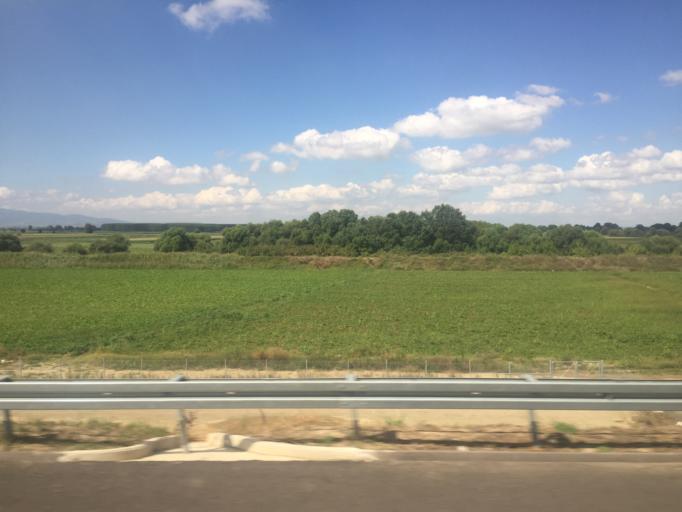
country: TR
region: Bursa
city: Tatkavakli
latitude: 40.1029
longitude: 28.2781
